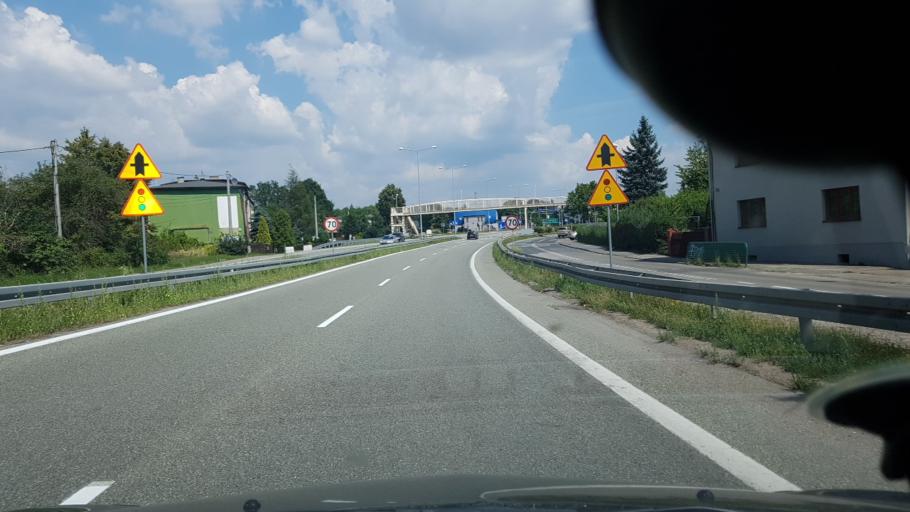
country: PL
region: Silesian Voivodeship
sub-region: Powiat mikolowski
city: Laziska Gorne
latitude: 50.1356
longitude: 18.8308
